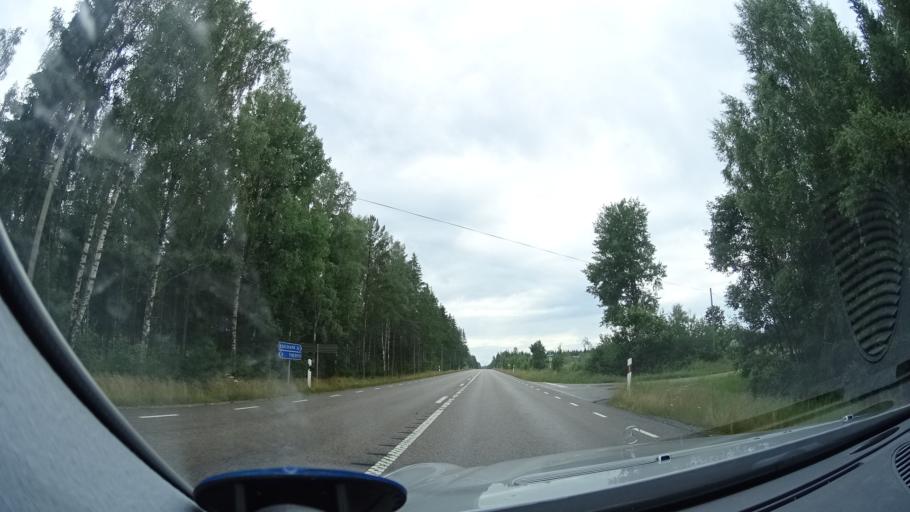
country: SE
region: Kronoberg
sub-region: Tingsryds Kommun
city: Tingsryd
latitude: 56.4584
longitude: 15.0004
